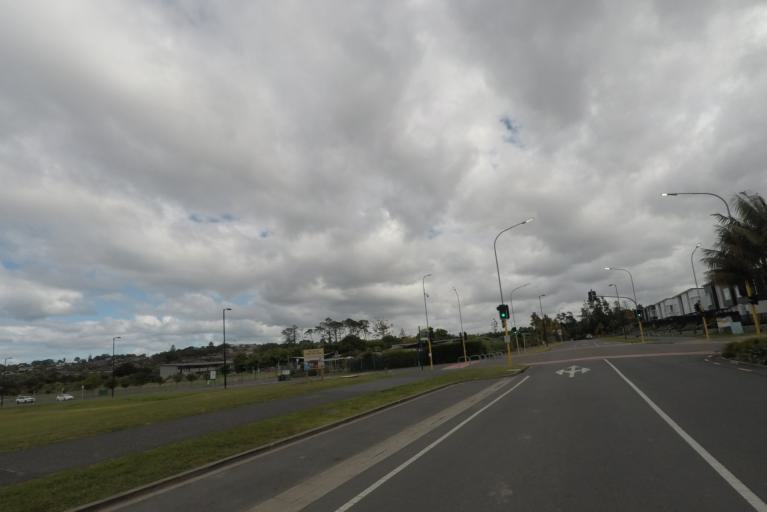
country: NZ
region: Auckland
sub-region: Auckland
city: Rothesay Bay
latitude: -36.6048
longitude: 174.6788
